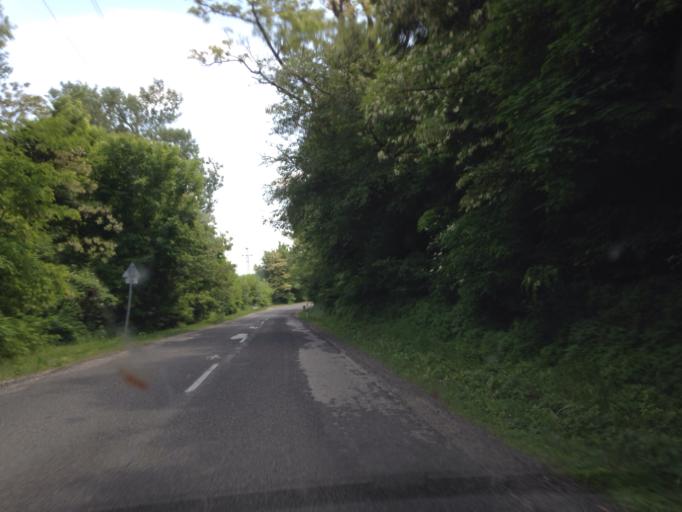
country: HU
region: Pest
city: Szob
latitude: 47.8119
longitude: 18.8334
